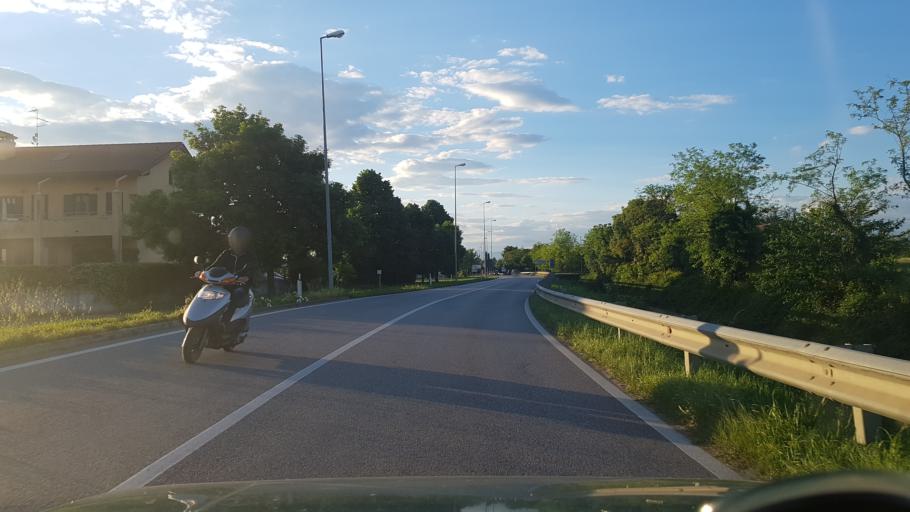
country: IT
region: Friuli Venezia Giulia
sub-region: Provincia di Udine
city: Santa Maria la Longa
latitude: 45.9286
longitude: 13.2929
